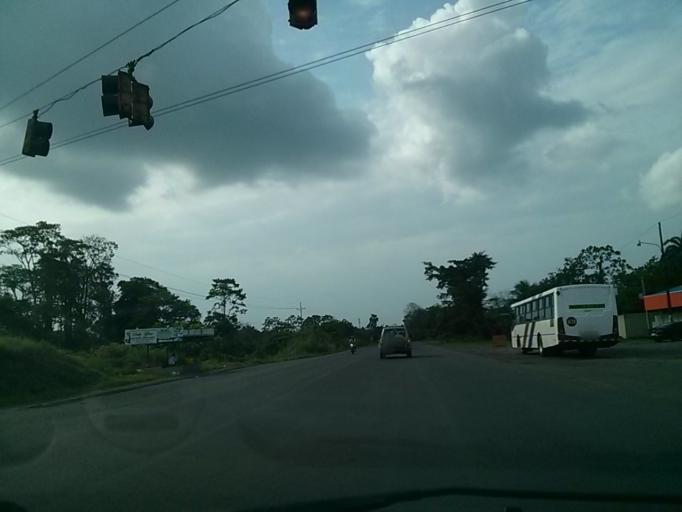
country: CR
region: Limon
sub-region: Canton de Siquirres
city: Siquirres
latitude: 10.1279
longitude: -83.5588
